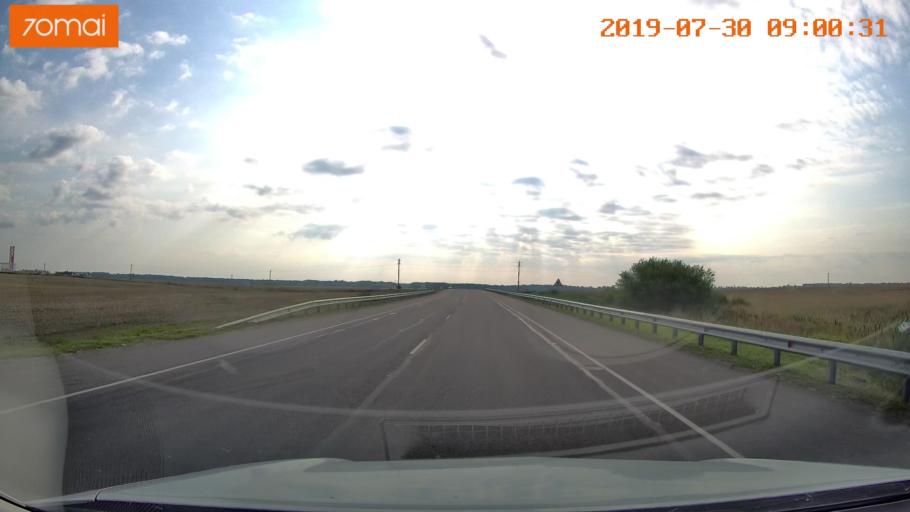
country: RU
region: Kaliningrad
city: Gusev
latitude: 54.6146
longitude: 22.1835
